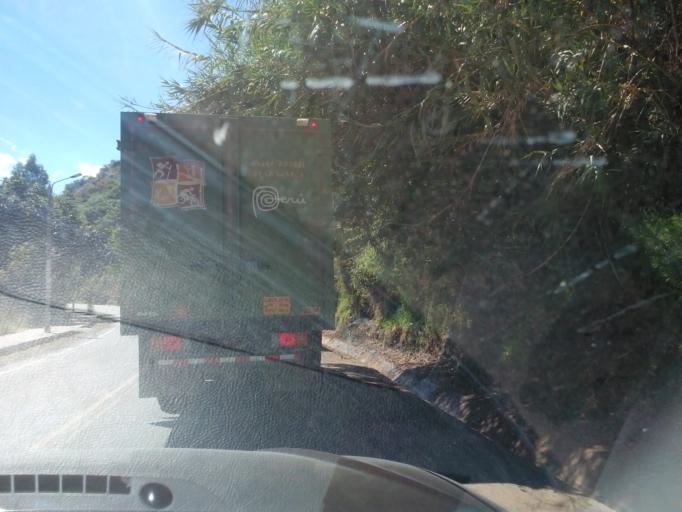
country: PE
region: Cusco
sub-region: Provincia de Anta
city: Limatambo
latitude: -13.4750
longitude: -72.4391
